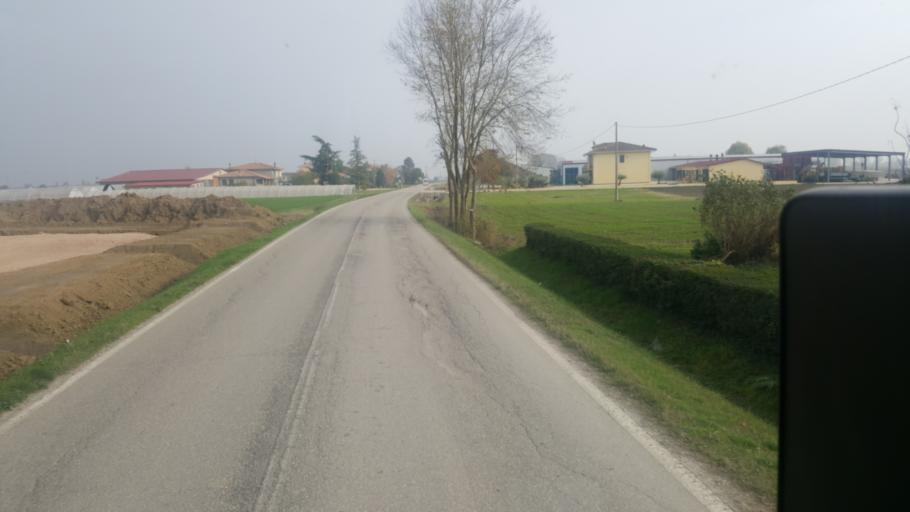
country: IT
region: Lombardy
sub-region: Provincia di Mantova
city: Sermide
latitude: 44.9589
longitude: 11.2532
